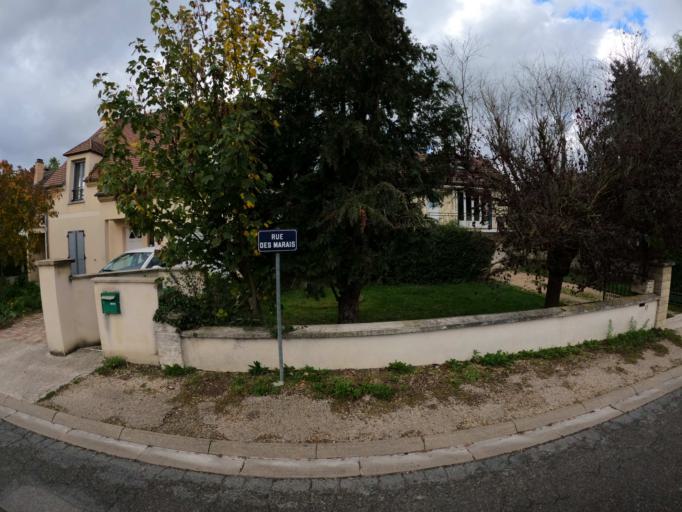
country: FR
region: Ile-de-France
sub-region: Departement de Seine-et-Marne
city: Coupvray
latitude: 48.8981
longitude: 2.7944
